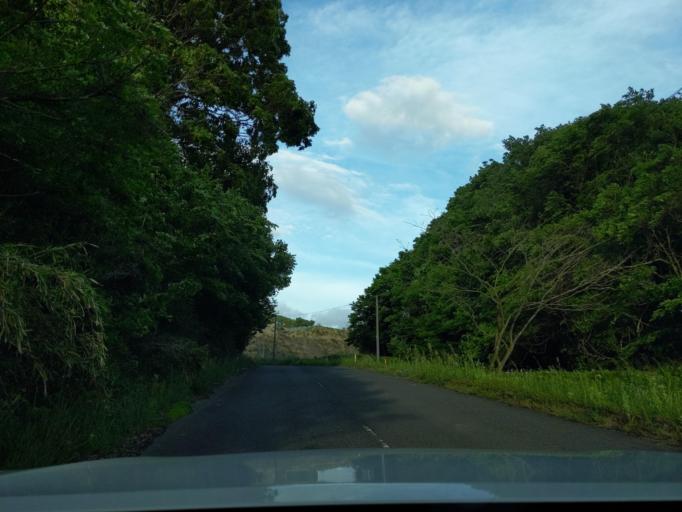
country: JP
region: Fukushima
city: Miharu
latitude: 37.4130
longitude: 140.4660
